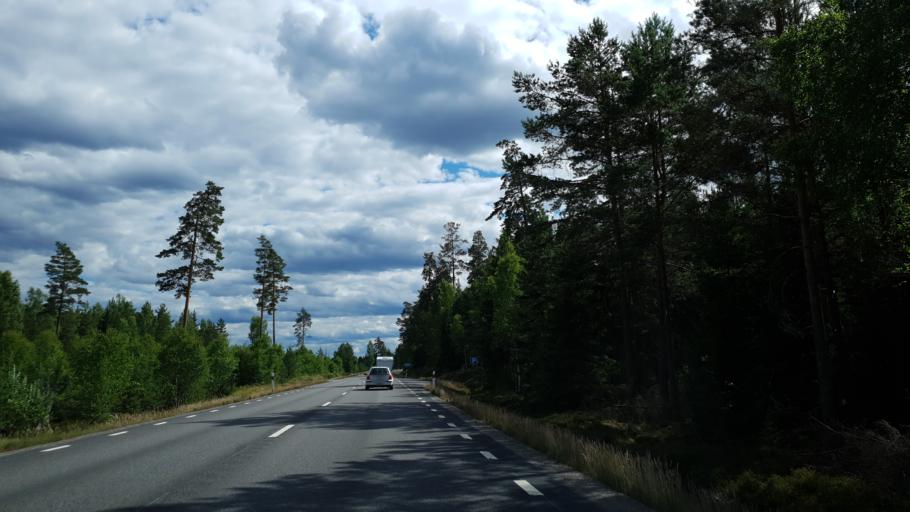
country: SE
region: Kronoberg
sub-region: Lessebo Kommun
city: Lessebo
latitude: 56.8075
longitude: 15.4121
